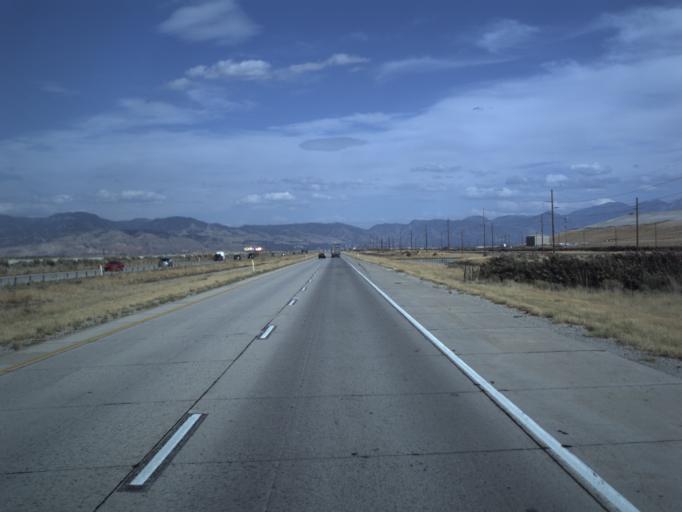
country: US
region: Utah
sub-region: Salt Lake County
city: Magna
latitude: 40.7707
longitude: -112.1165
